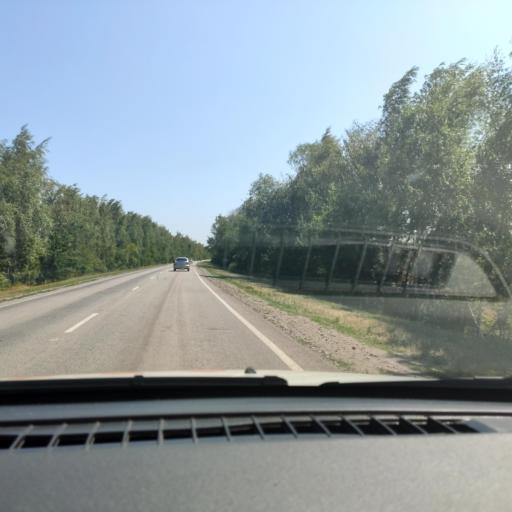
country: RU
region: Voronezj
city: Liski
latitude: 50.8016
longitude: 39.3331
